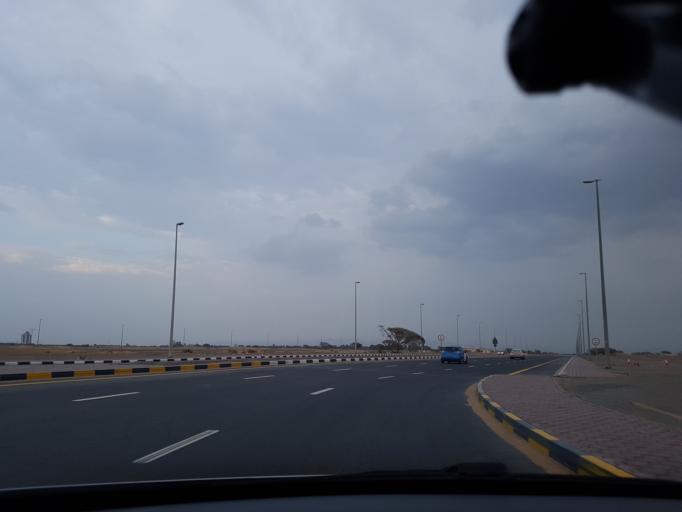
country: AE
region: Ash Shariqah
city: Adh Dhayd
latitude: 25.2673
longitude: 55.8995
